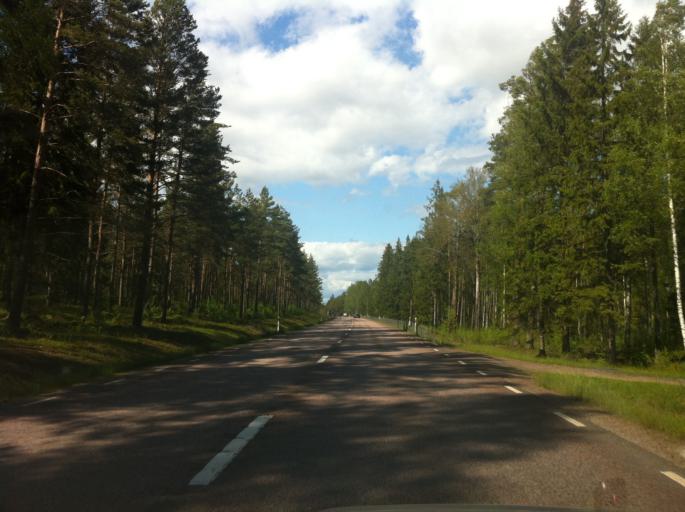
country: SE
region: Vaermland
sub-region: Kristinehamns Kommun
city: Bjorneborg
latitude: 59.1933
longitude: 14.1828
